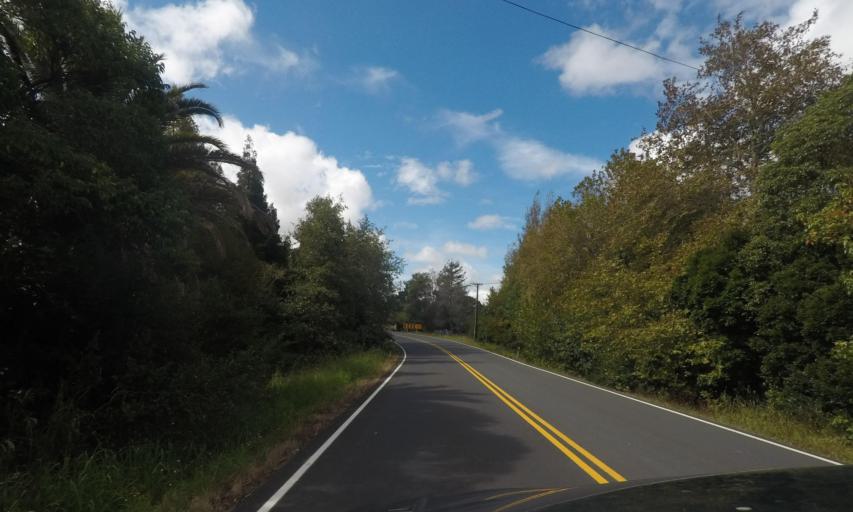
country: NZ
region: Auckland
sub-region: Auckland
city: Rosebank
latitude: -36.7978
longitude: 174.6355
